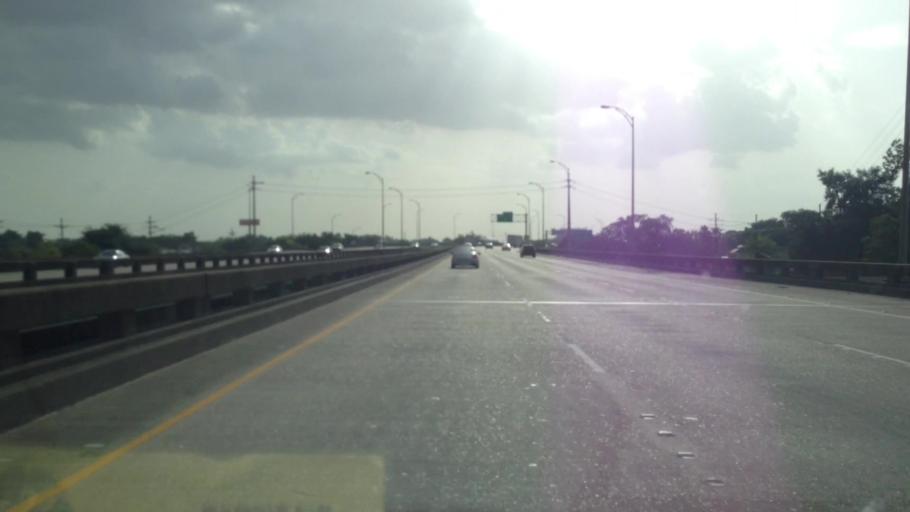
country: US
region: Louisiana
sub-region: Orleans Parish
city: New Orleans
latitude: 29.9909
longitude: -90.0671
